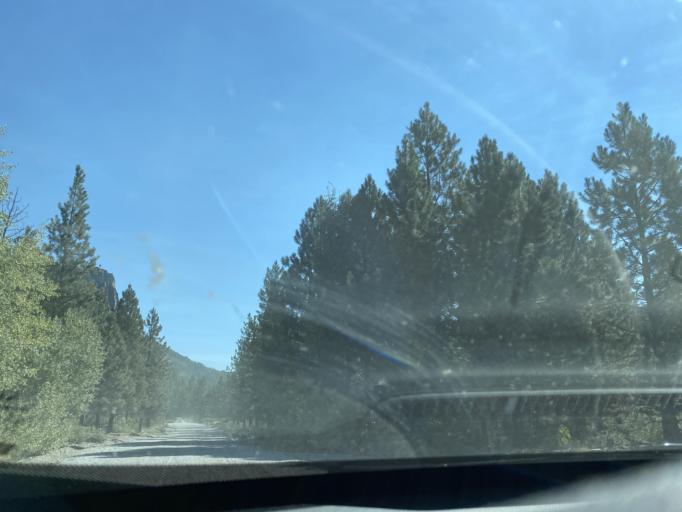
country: US
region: Oregon
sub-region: Deschutes County
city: Sunriver
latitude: 44.0306
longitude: -121.5575
